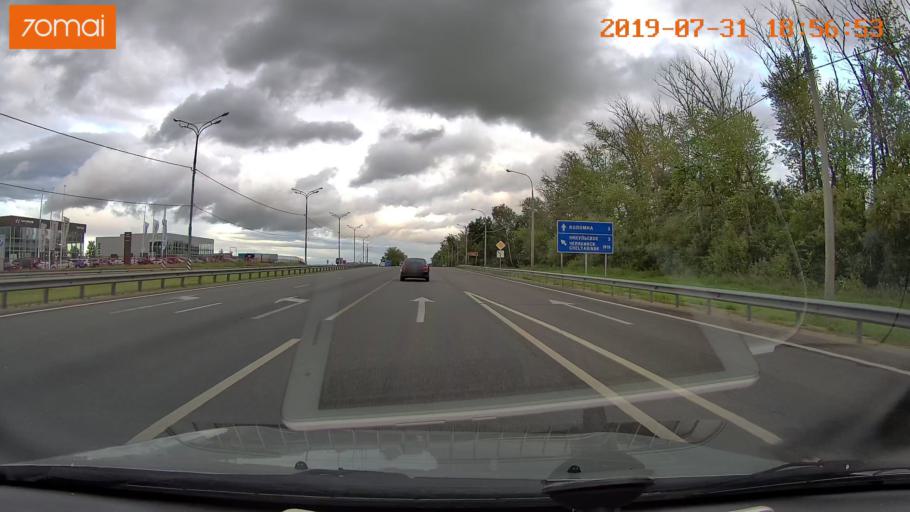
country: RU
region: Moskovskaya
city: Raduzhnyy
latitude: 55.1589
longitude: 38.6844
